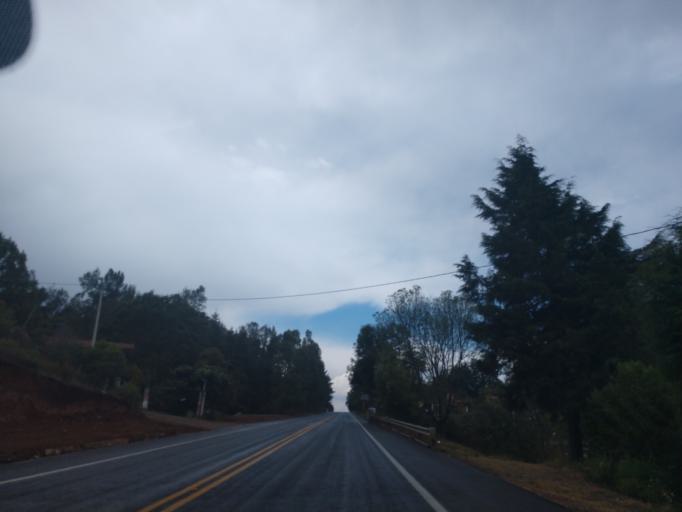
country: MX
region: Jalisco
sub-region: Mazamitla
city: Mazamitla
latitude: 19.9447
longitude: -103.0658
